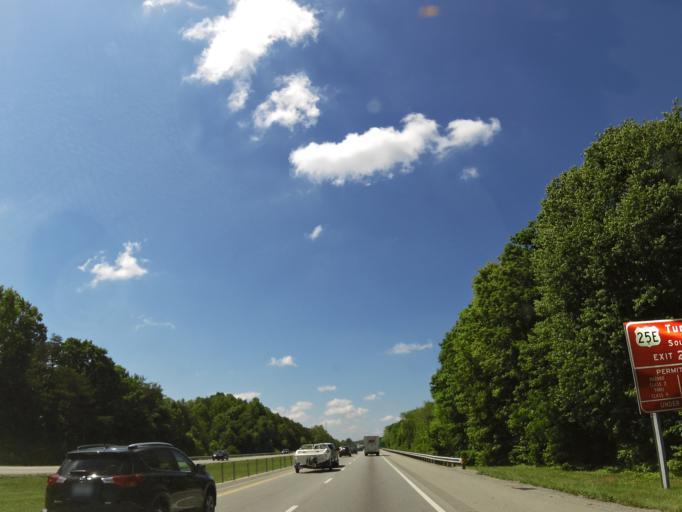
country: US
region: Kentucky
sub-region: Laurel County
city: North Corbin
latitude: 37.0118
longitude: -84.1025
